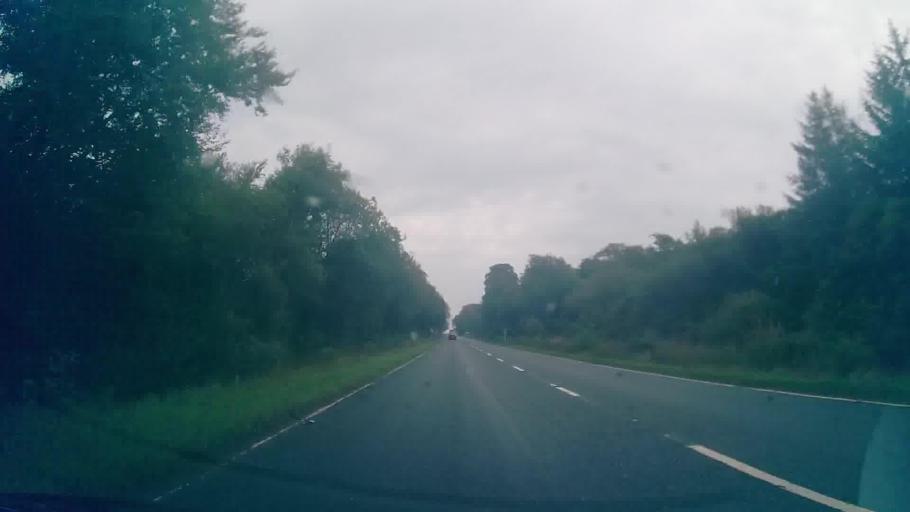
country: GB
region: Scotland
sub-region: Dumfries and Galloway
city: Annan
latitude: 55.0098
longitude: -3.3414
